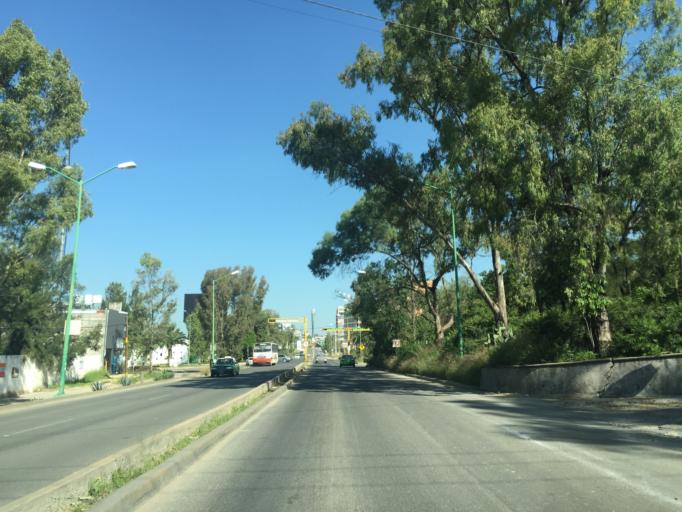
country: MX
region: Guanajuato
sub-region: Leon
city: La Ermita
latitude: 21.1679
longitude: -101.7299
